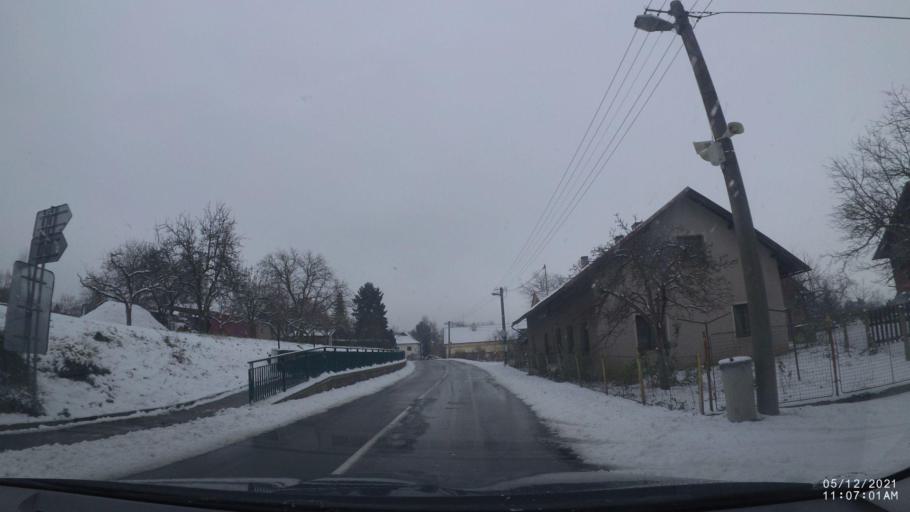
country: CZ
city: Solnice
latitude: 50.1807
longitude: 16.2228
